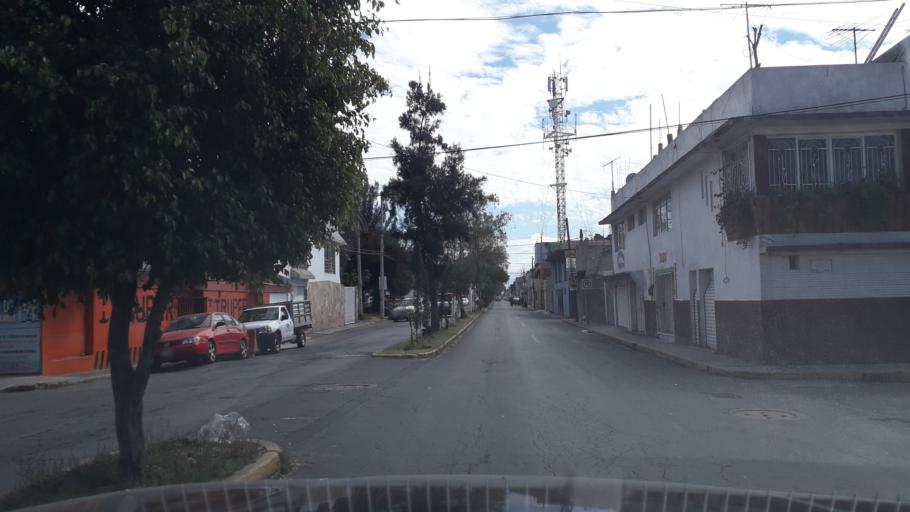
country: MX
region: Mexico City
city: Gustavo A. Madero
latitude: 19.5095
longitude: -99.0877
